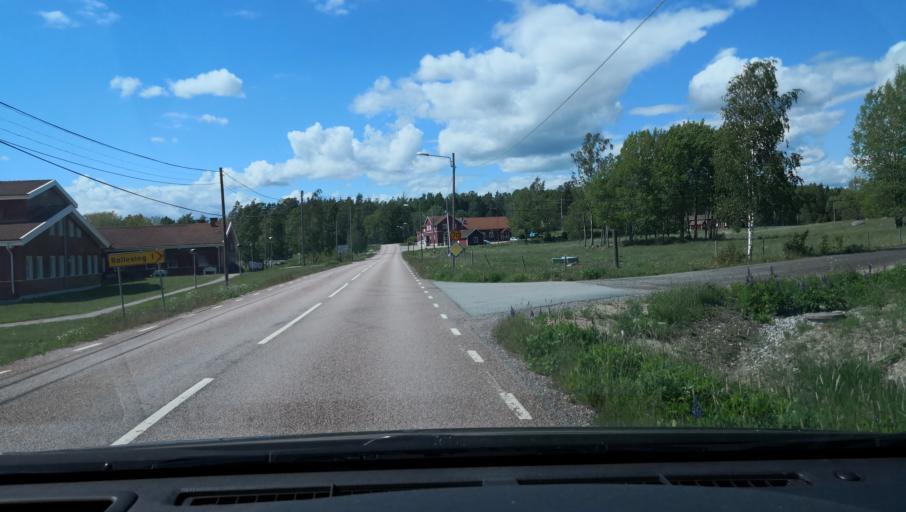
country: SE
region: Vaestmanland
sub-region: Arboga Kommun
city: Tyringe
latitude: 59.2929
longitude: 16.0483
